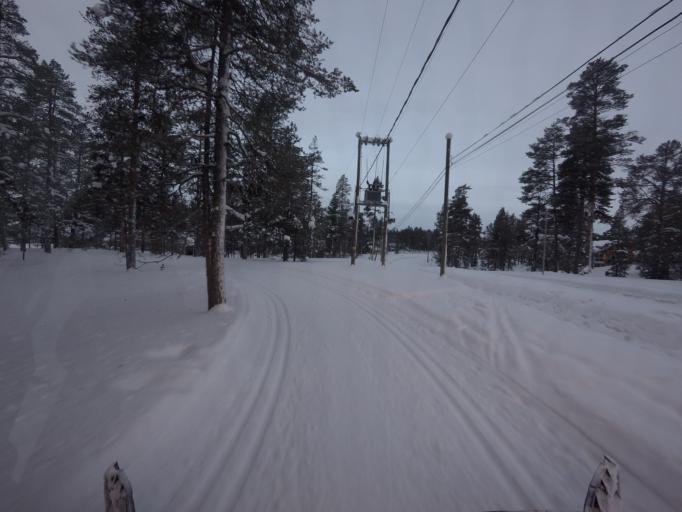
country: FI
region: Lapland
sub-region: Tunturi-Lappi
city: Kolari
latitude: 67.6233
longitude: 24.1520
